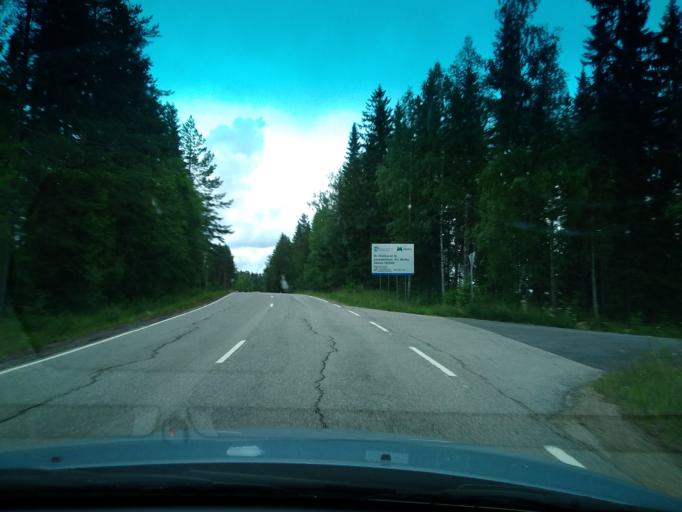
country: FI
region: Central Finland
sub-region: Keuruu
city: Multia
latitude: 62.4163
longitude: 24.7843
